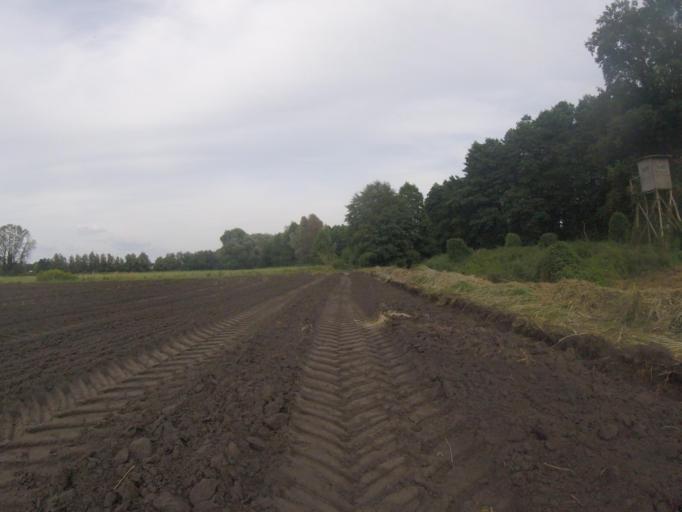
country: DE
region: Brandenburg
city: Rangsdorf
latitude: 52.3178
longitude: 13.4617
